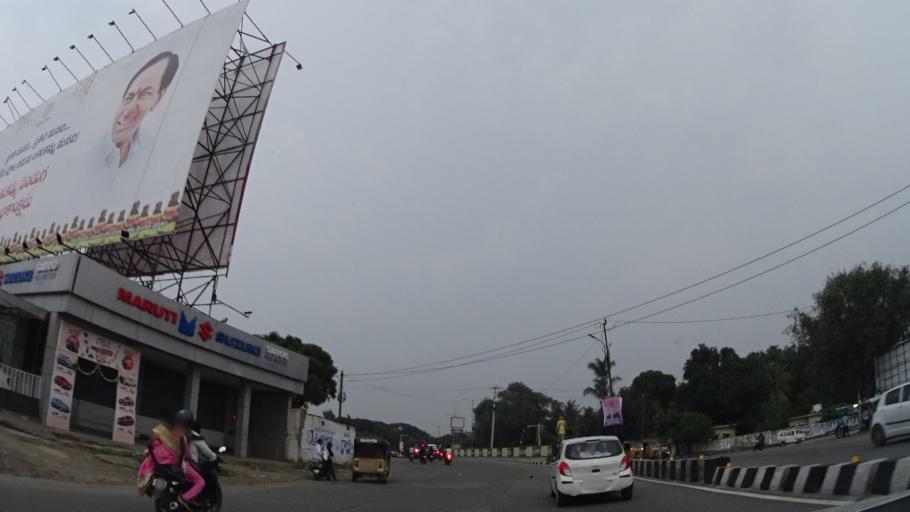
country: IN
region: Telangana
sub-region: Hyderabad
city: Malkajgiri
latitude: 17.4521
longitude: 78.4861
